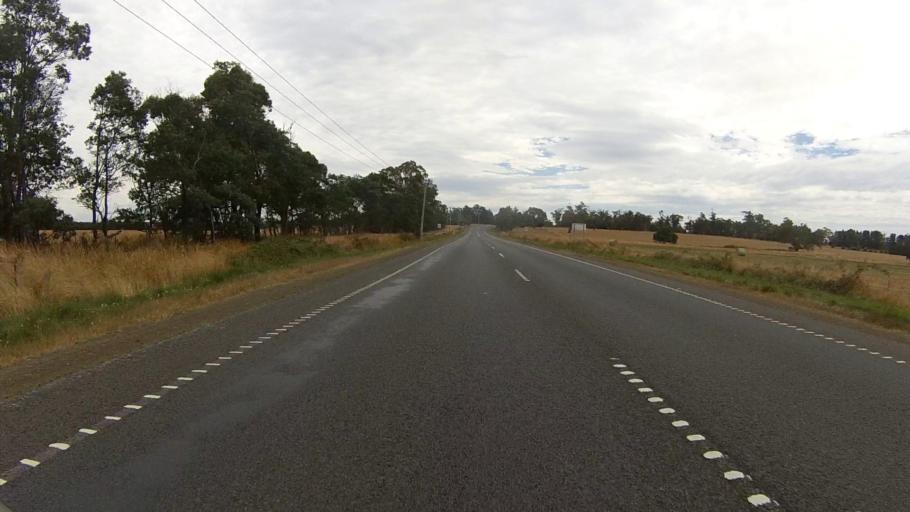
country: AU
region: Tasmania
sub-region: Northern Midlands
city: Evandale
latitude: -41.6087
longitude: 147.2194
